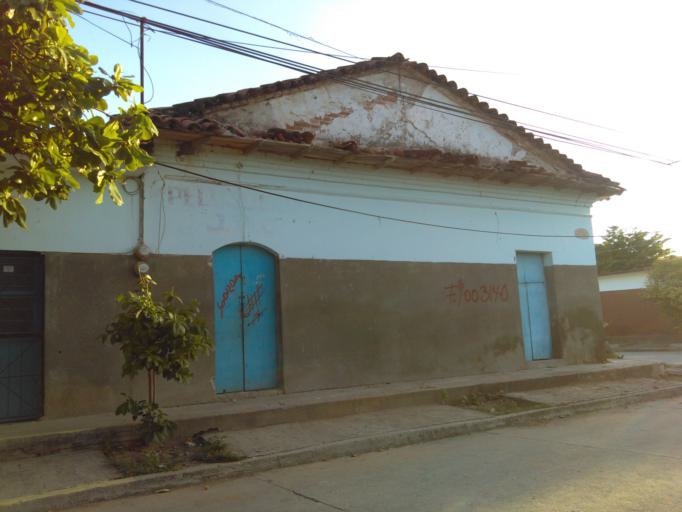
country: MX
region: Oaxaca
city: San Jeronimo Ixtepec
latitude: 16.5680
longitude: -95.1011
